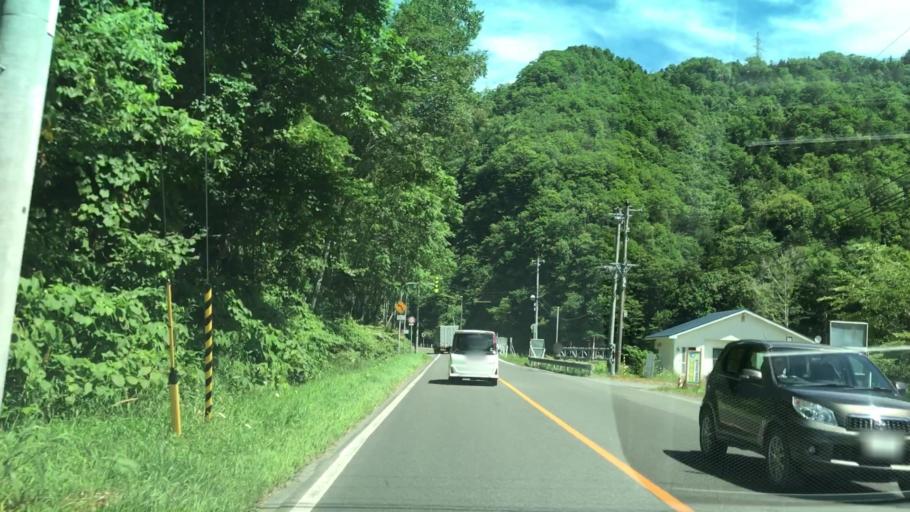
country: JP
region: Hokkaido
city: Shimo-furano
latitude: 42.9124
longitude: 142.5866
